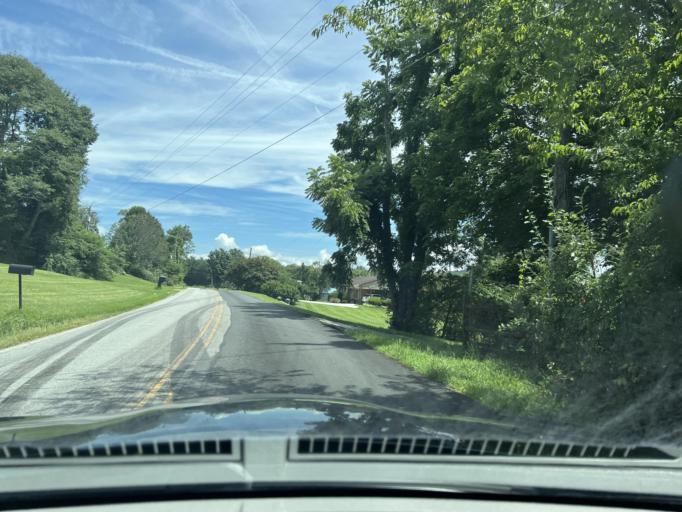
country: US
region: North Carolina
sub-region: Henderson County
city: Edneyville
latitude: 35.3899
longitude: -82.3623
